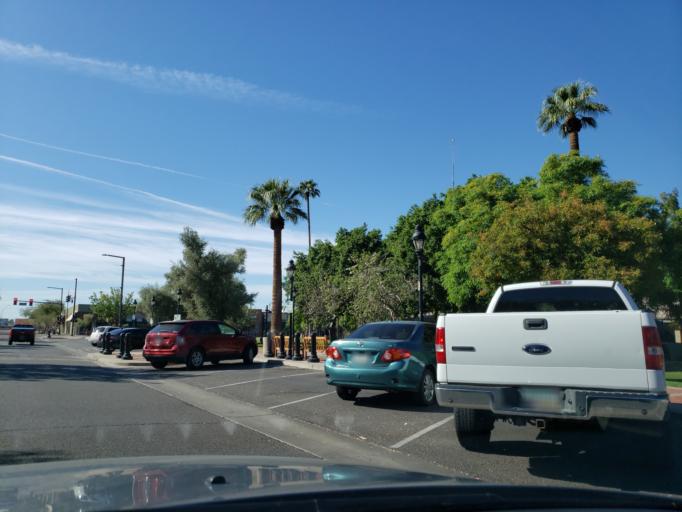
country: US
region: Arizona
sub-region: Maricopa County
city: Glendale
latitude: 33.5395
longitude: -112.1837
